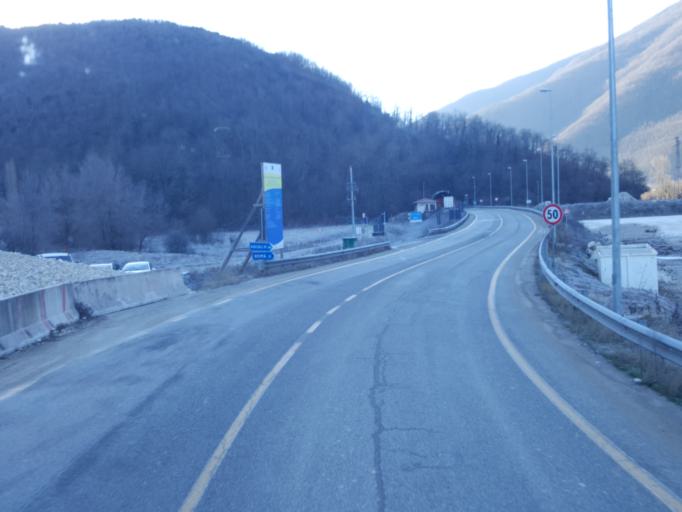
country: IT
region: Latium
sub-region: Provincia di Rieti
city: Colli sul Velino
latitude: 42.5053
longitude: 12.7465
